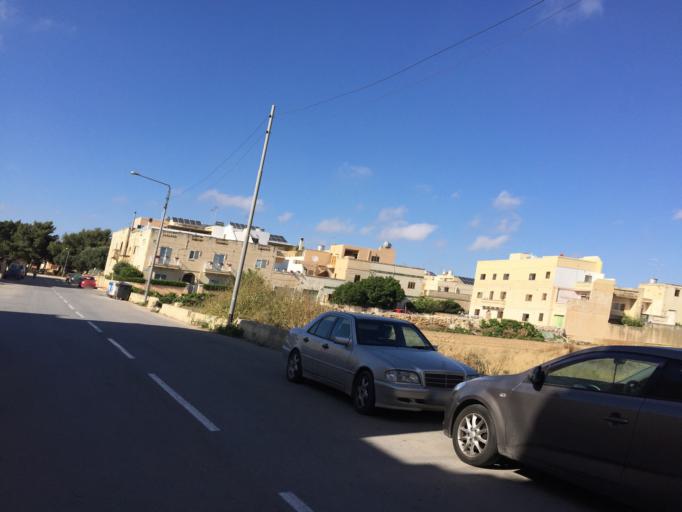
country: MT
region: Il-Qrendi
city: Qrendi
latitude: 35.8363
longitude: 14.4613
